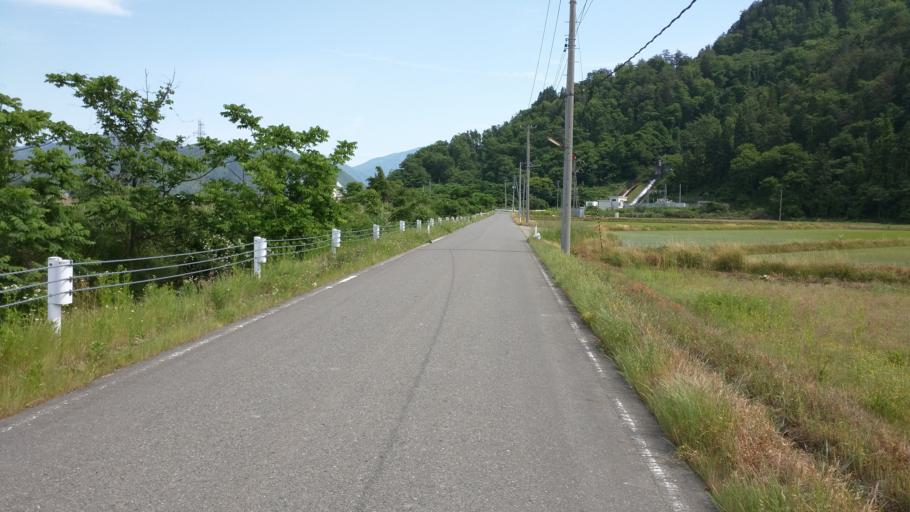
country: JP
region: Fukushima
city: Kitakata
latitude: 37.4490
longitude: 139.9035
